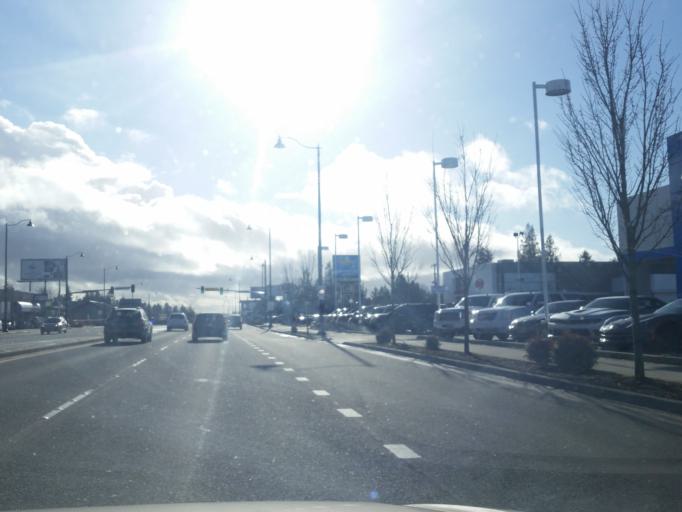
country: US
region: Washington
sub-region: King County
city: Shoreline
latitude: 47.7537
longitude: -122.3457
